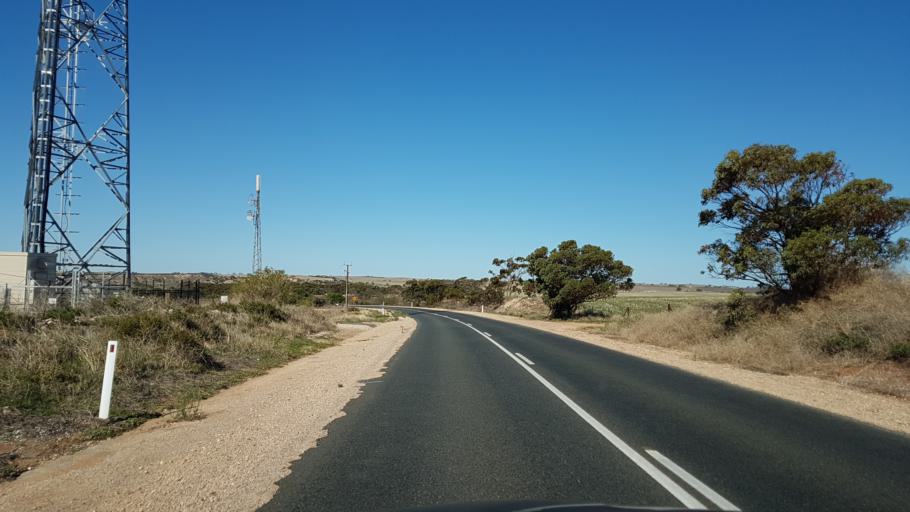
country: AU
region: South Australia
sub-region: Mid Murray
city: Mannum
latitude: -34.7579
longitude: 139.5487
